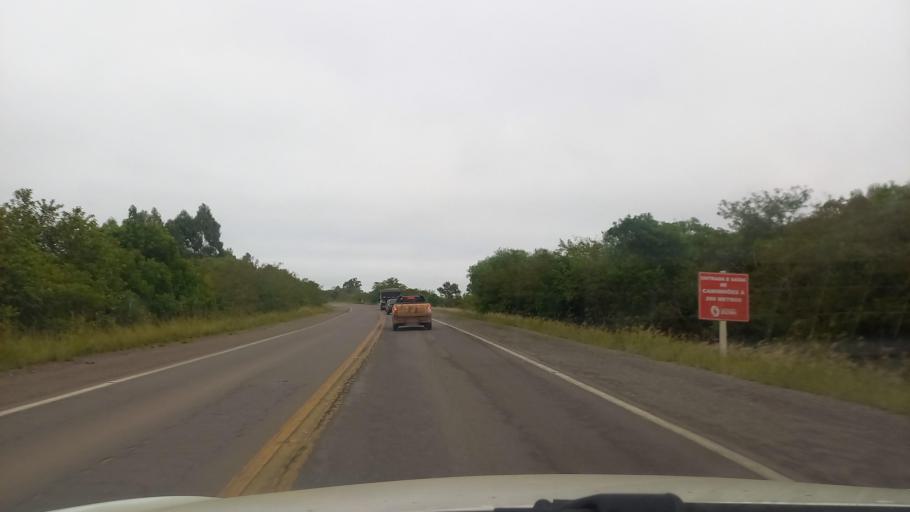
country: BR
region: Rio Grande do Sul
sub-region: Sao Pedro Do Sul
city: Sao Pedro do Sul
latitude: -29.7705
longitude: -54.0935
